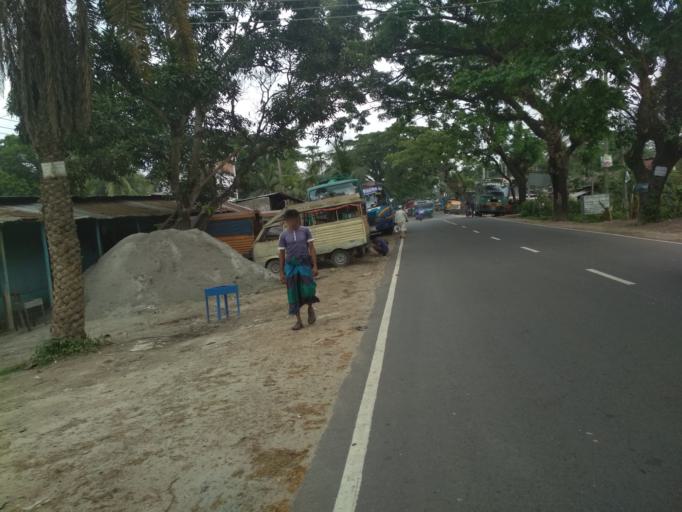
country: BD
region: Chittagong
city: Lakshmipur
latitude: 22.9421
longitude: 90.8441
